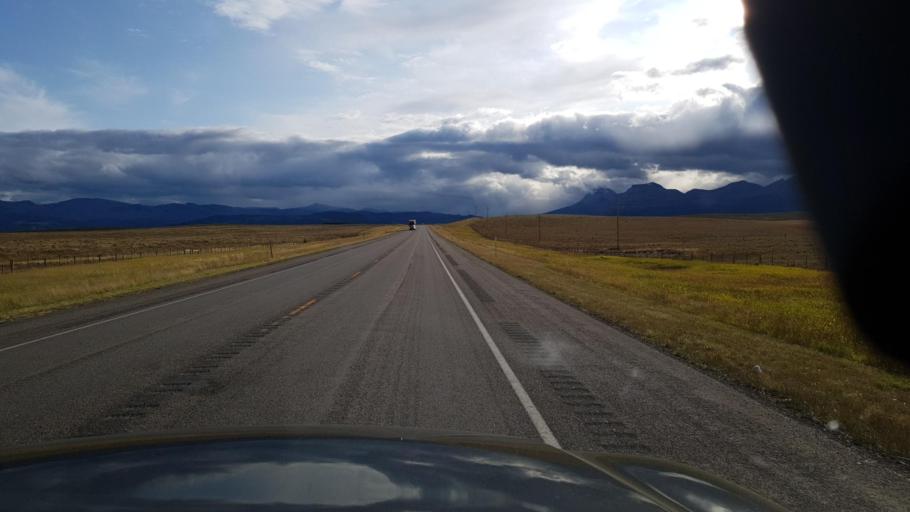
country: US
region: Montana
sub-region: Glacier County
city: South Browning
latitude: 48.4776
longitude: -113.1424
